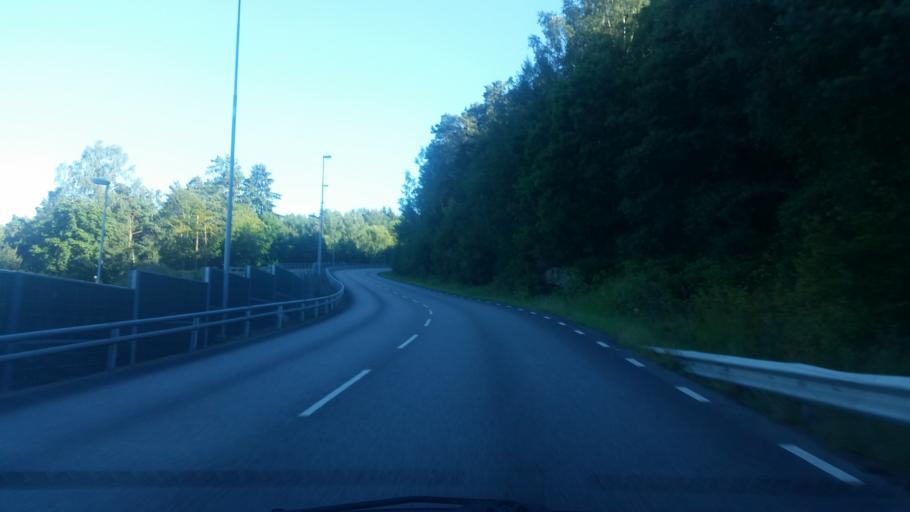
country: SE
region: Vaestra Goetaland
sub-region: Partille Kommun
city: Furulund
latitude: 57.7375
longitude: 12.1330
